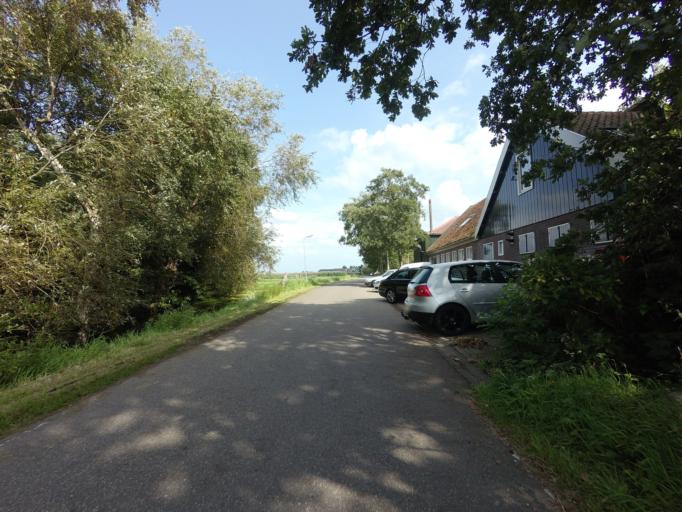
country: NL
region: North Holland
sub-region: Gemeente Waterland
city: Broek in Waterland
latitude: 52.4537
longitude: 4.9960
